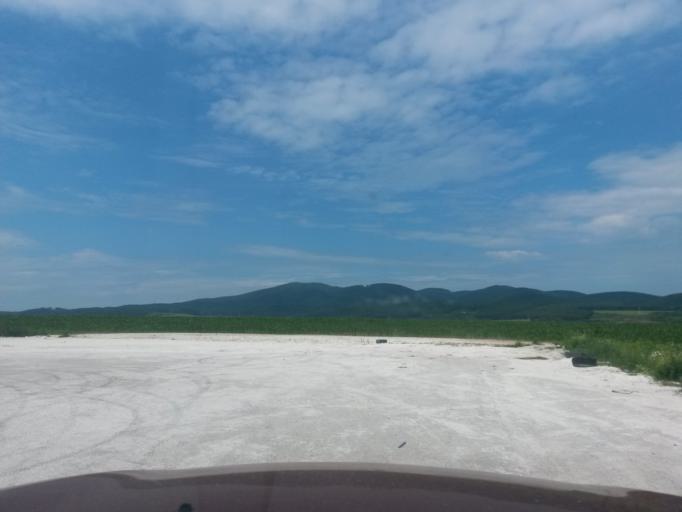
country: SK
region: Kosicky
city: Secovce
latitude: 48.6239
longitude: 21.5092
